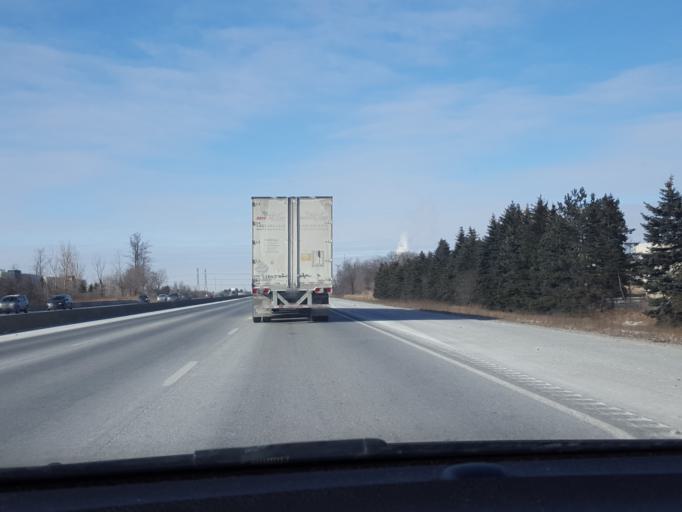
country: CA
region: Ontario
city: Brampton
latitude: 43.6017
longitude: -79.7715
